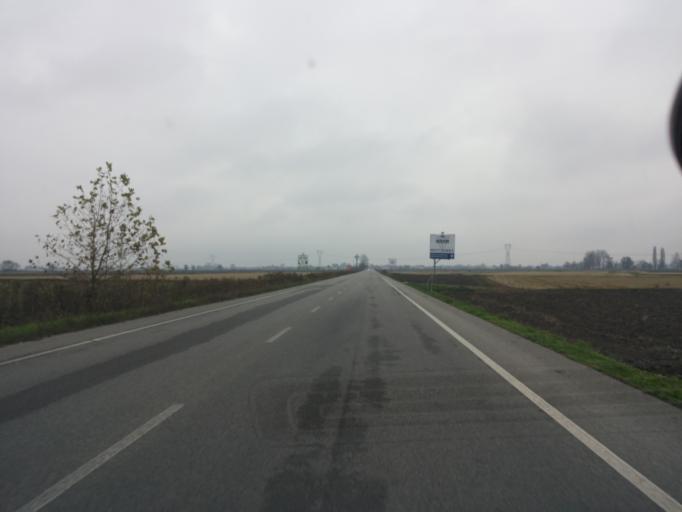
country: IT
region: Piedmont
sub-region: Provincia di Alessandria
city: Villanova Monferrato
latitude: 45.1998
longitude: 8.4646
